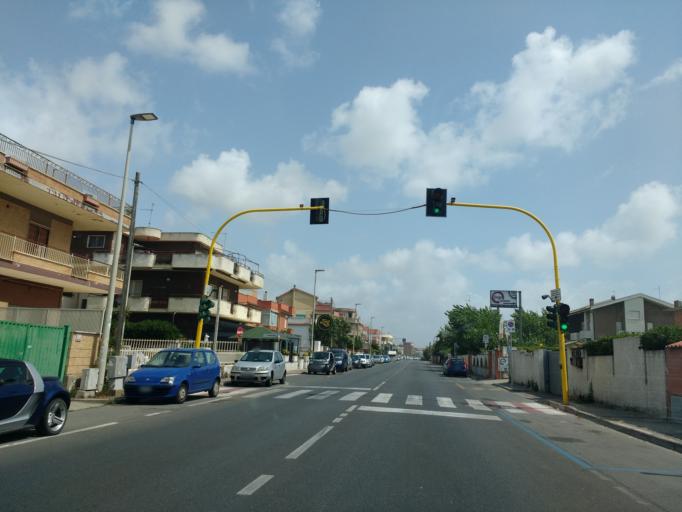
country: IT
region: Latium
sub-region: Citta metropolitana di Roma Capitale
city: Torvaianica
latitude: 41.6461
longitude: 12.4317
